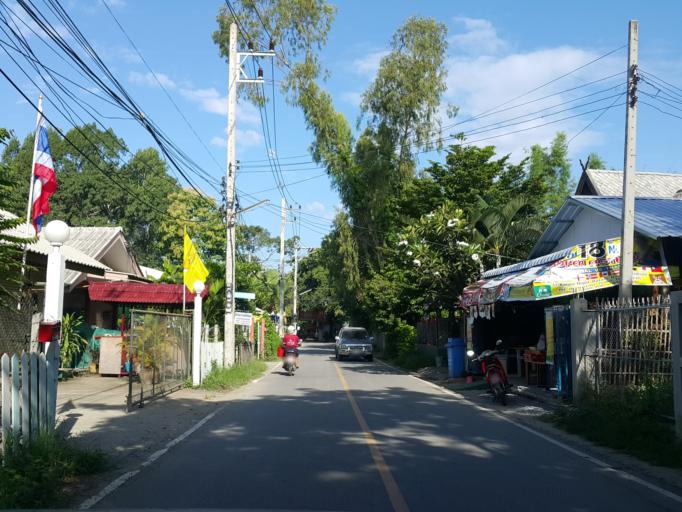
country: TH
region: Chiang Mai
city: San Kamphaeng
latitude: 18.7758
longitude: 99.0828
